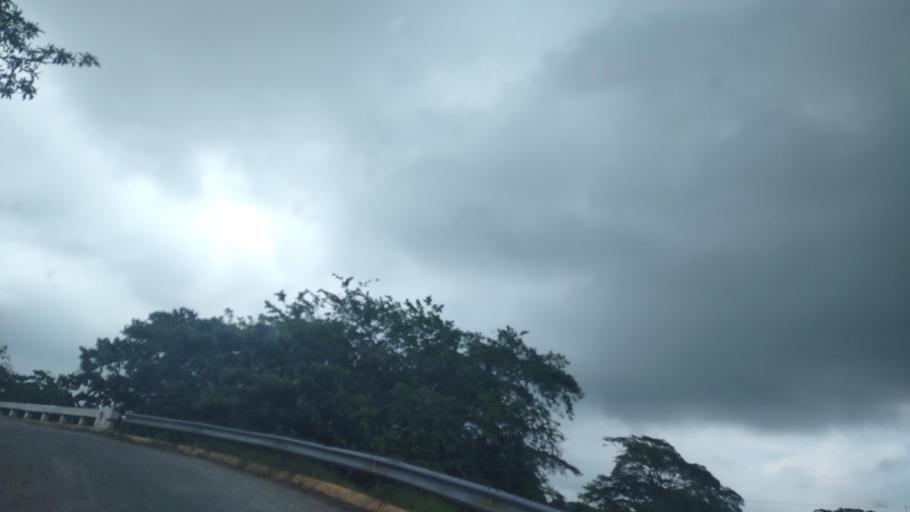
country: MX
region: Veracruz
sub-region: Uxpanapa
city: Poblado 10
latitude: 17.4942
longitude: -94.1644
